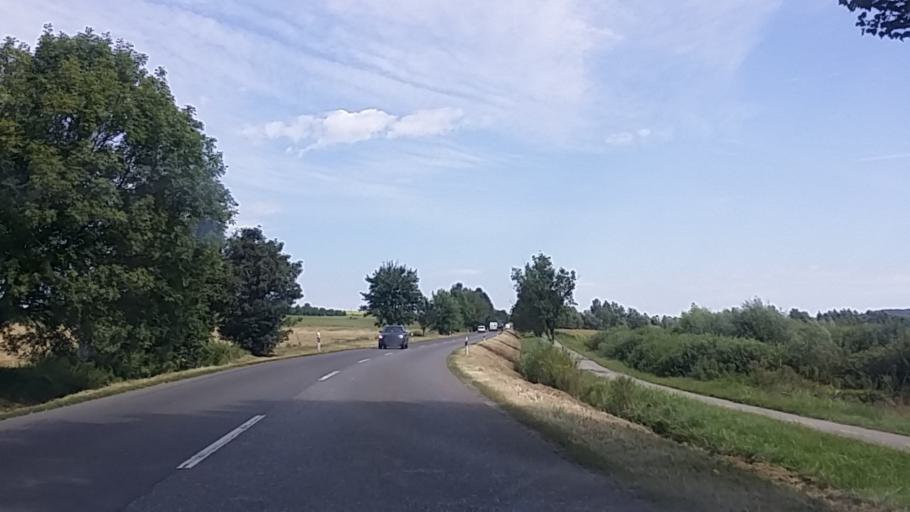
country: HU
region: Baranya
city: Sasd
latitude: 46.2961
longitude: 18.1232
